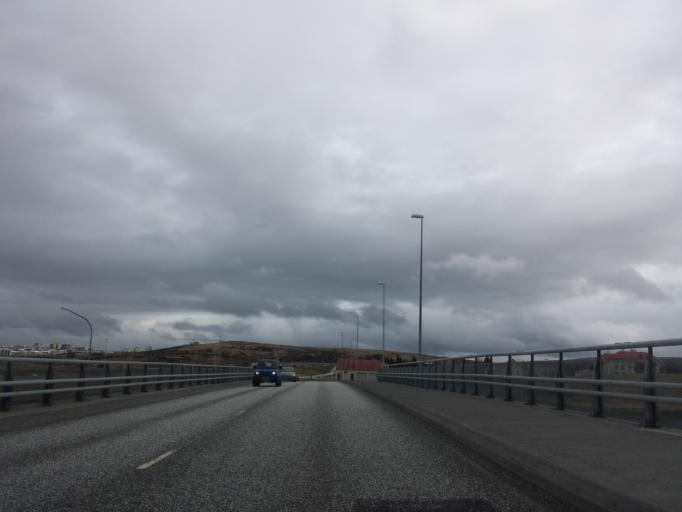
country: IS
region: Capital Region
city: Gardabaer
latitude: 64.0833
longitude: -21.8952
